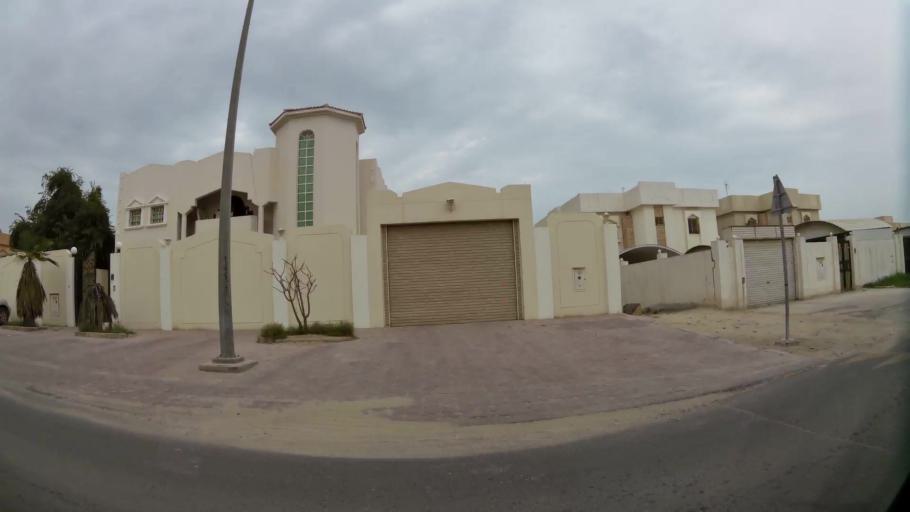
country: QA
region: Baladiyat ar Rayyan
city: Ar Rayyan
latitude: 25.3392
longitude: 51.4664
